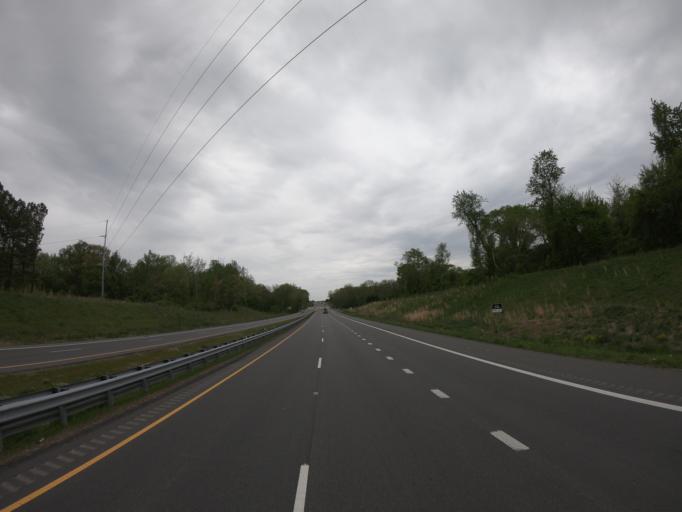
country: US
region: Maryland
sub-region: Caroline County
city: Ridgely
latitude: 38.9232
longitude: -75.9532
